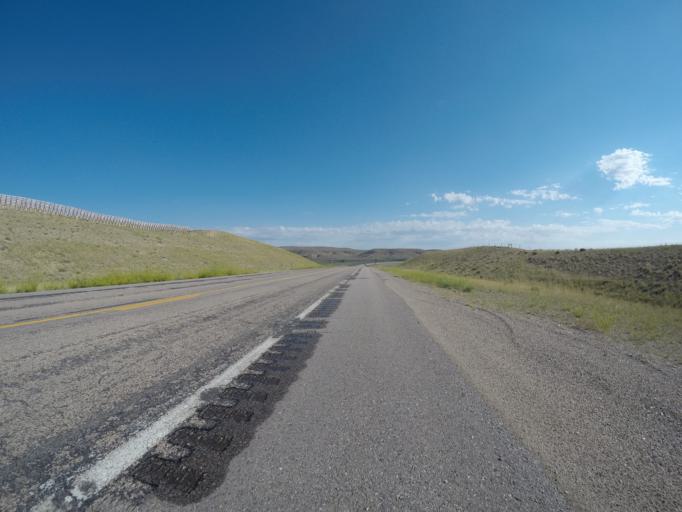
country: US
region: Wyoming
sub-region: Lincoln County
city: Kemmerer
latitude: 42.0784
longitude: -110.1604
